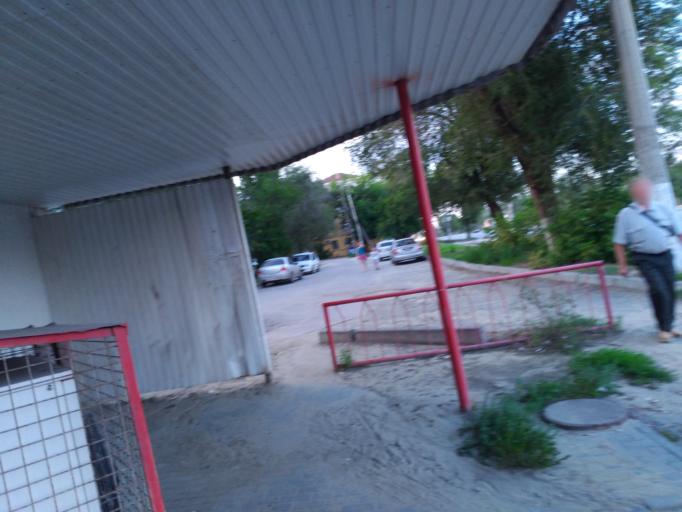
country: RU
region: Volgograd
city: Volgograd
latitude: 48.6630
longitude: 44.4510
